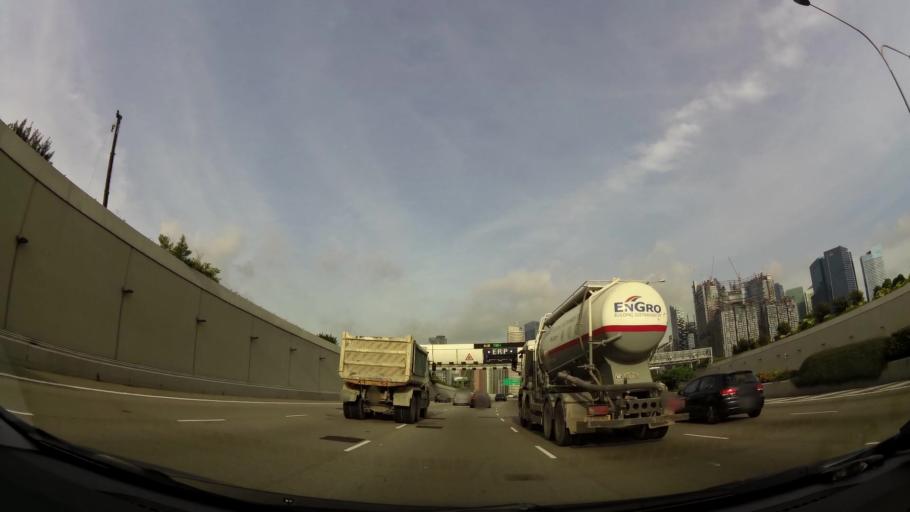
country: SG
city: Singapore
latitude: 1.2705
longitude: 103.8570
